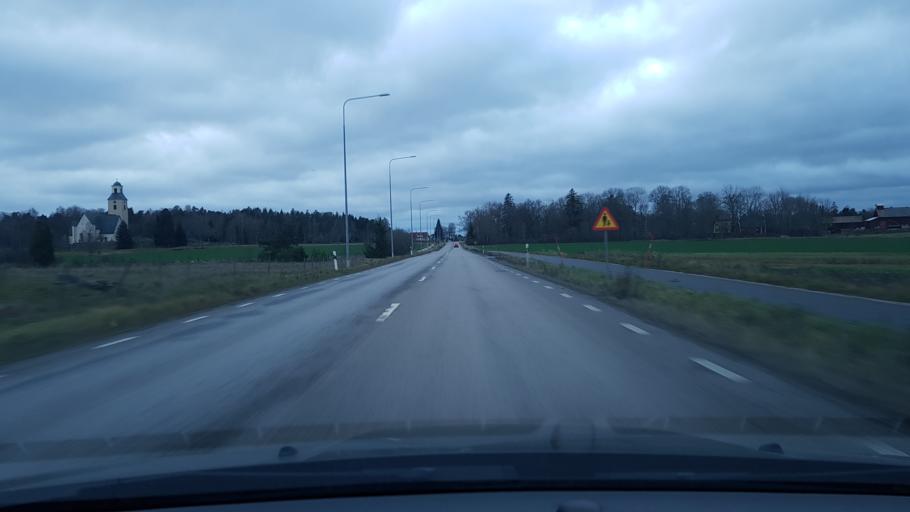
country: SE
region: Uppsala
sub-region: Uppsala Kommun
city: Vattholma
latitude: 59.9515
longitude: 17.8873
